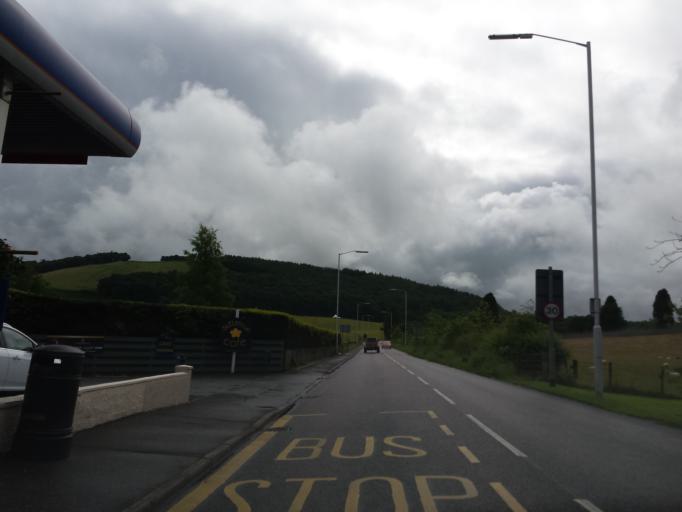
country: GB
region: Scotland
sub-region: Fife
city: Newburgh
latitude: 56.3505
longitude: -3.2290
